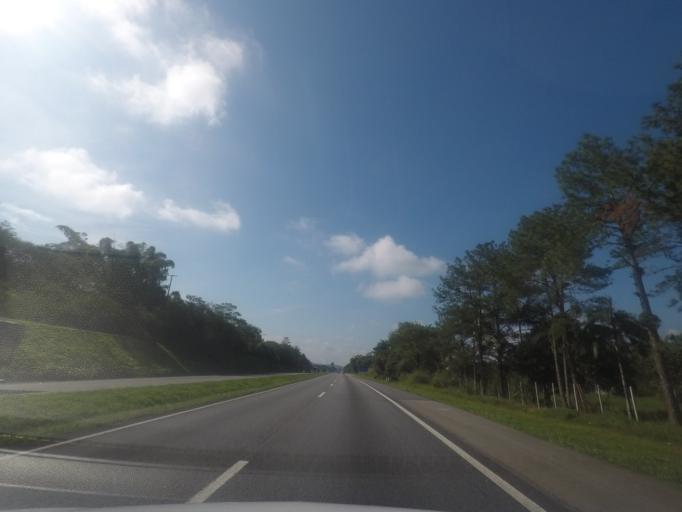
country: BR
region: Parana
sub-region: Paranagua
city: Paranagua
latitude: -25.5609
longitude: -48.6466
